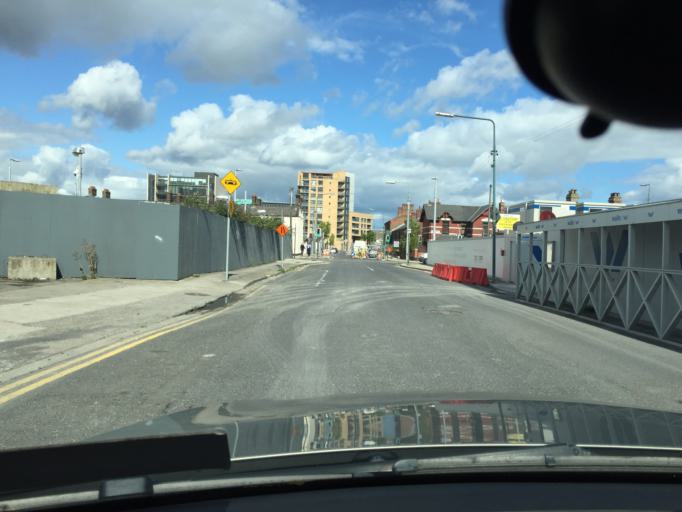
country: IE
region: Leinster
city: Ringsend
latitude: 53.3481
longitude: -6.2354
